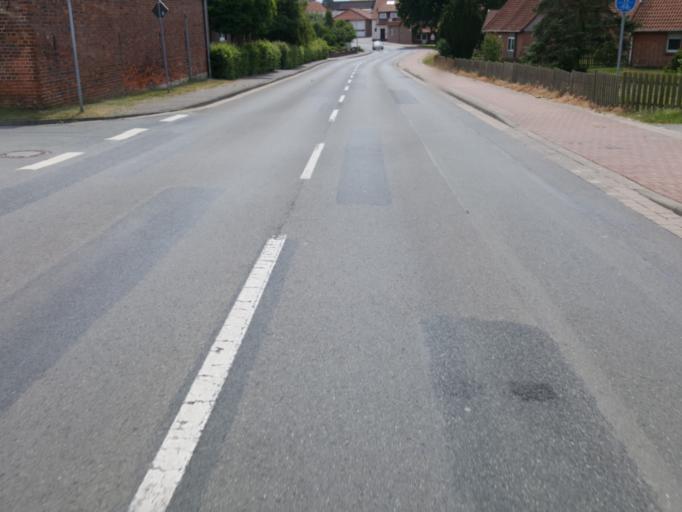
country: DE
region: Lower Saxony
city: Husum
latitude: 52.5920
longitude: 9.2475
